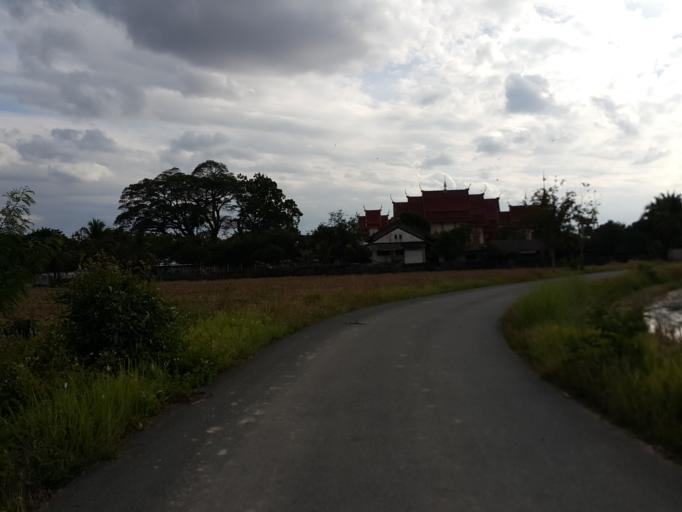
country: TH
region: Chiang Mai
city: San Sai
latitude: 18.8717
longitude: 99.1103
